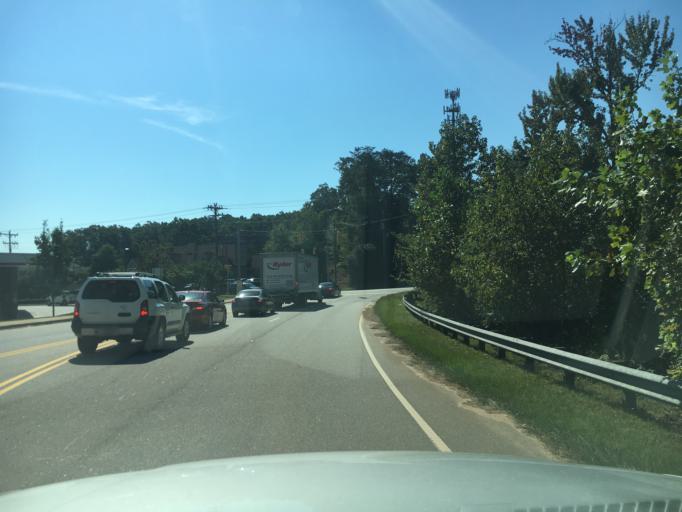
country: US
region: South Carolina
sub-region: Greenville County
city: Taylors
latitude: 34.8633
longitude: -82.2795
